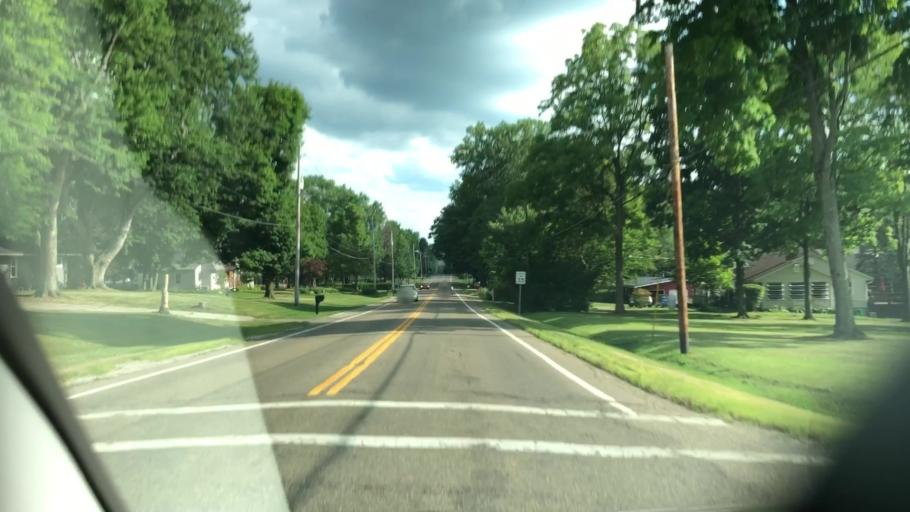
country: US
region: Ohio
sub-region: Summit County
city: Fairlawn
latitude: 41.0944
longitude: -81.6446
